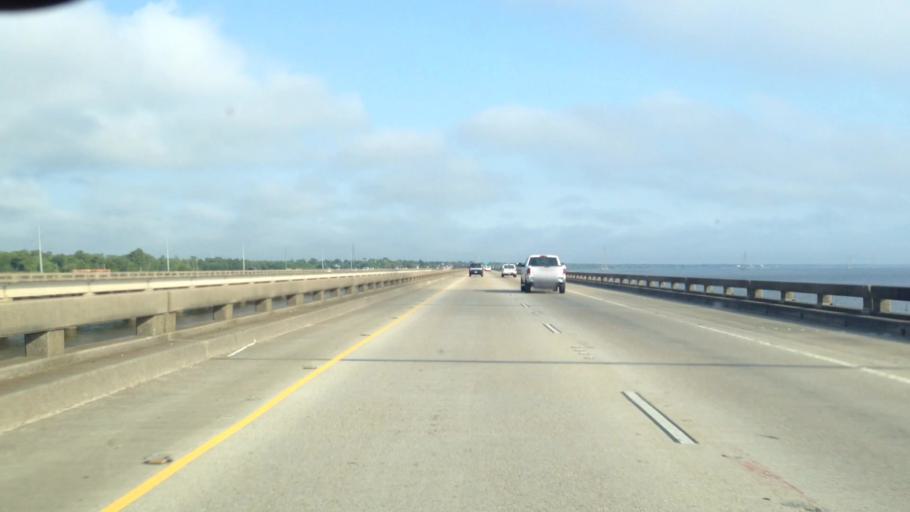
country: US
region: Louisiana
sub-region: Saint Charles Parish
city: Norco
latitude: 30.0681
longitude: -90.3900
